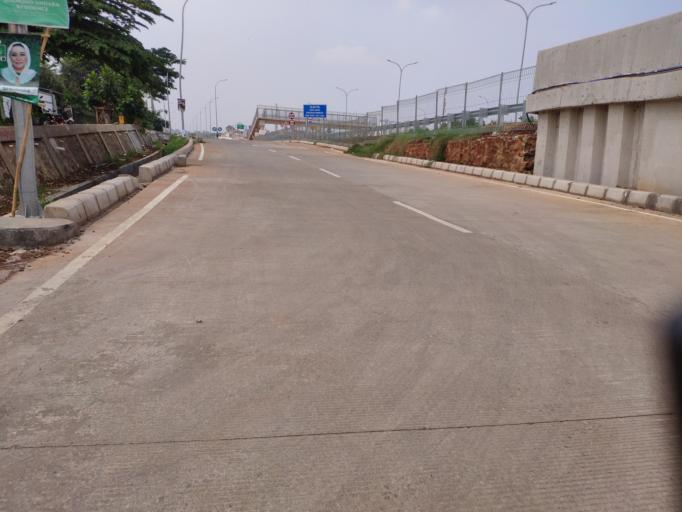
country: ID
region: West Java
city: Pamulang
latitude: -6.3265
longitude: 106.8018
